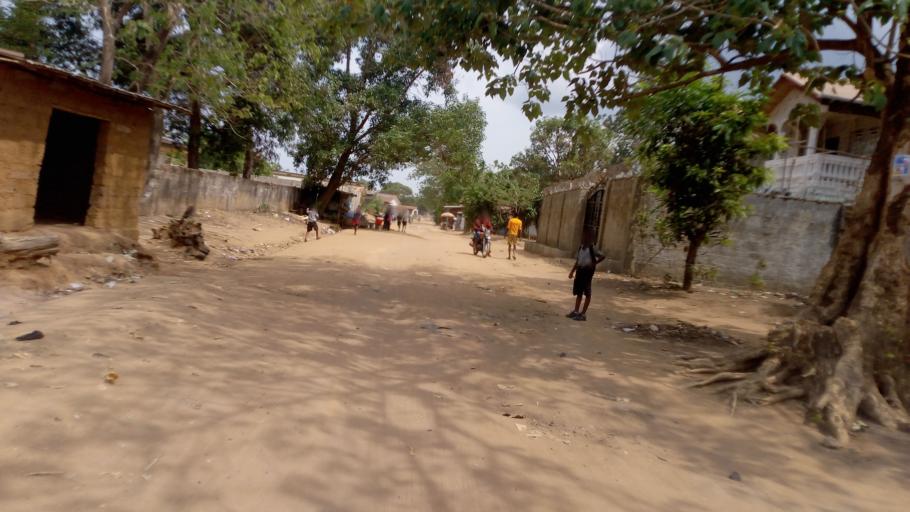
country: SL
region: Western Area
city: Waterloo
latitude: 8.3165
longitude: -13.0651
